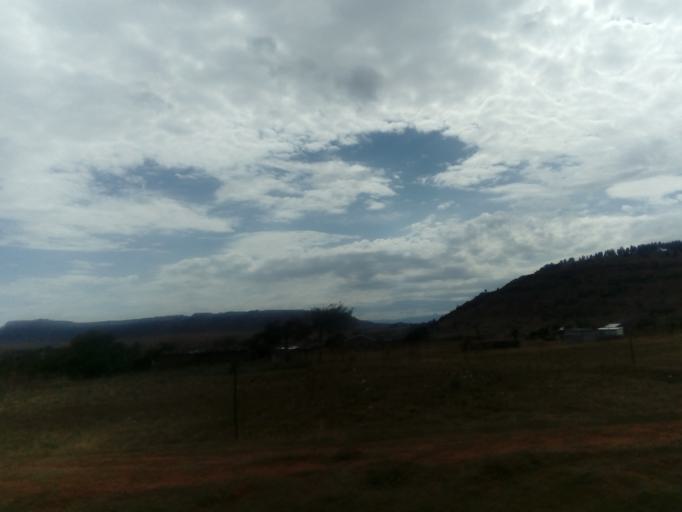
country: LS
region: Leribe
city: Maputsoe
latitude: -28.9497
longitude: 27.9596
